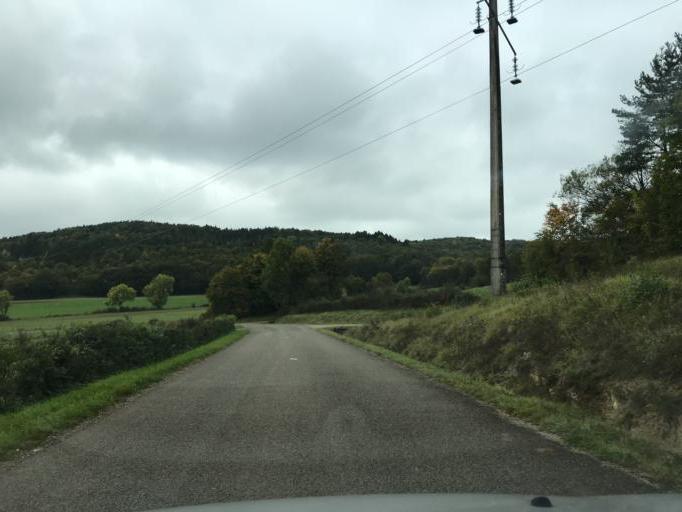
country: FR
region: Franche-Comte
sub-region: Departement du Jura
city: Arinthod
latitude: 46.4314
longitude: 5.4740
